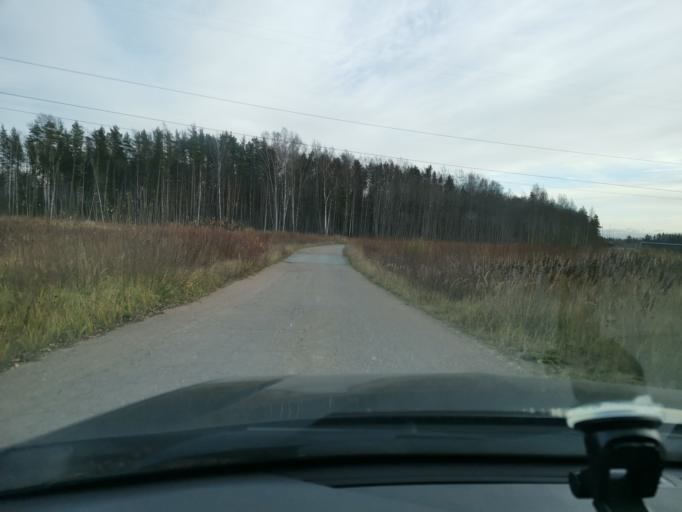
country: EE
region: Ida-Virumaa
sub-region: Sillamaee linn
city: Sillamae
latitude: 59.2632
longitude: 27.9039
